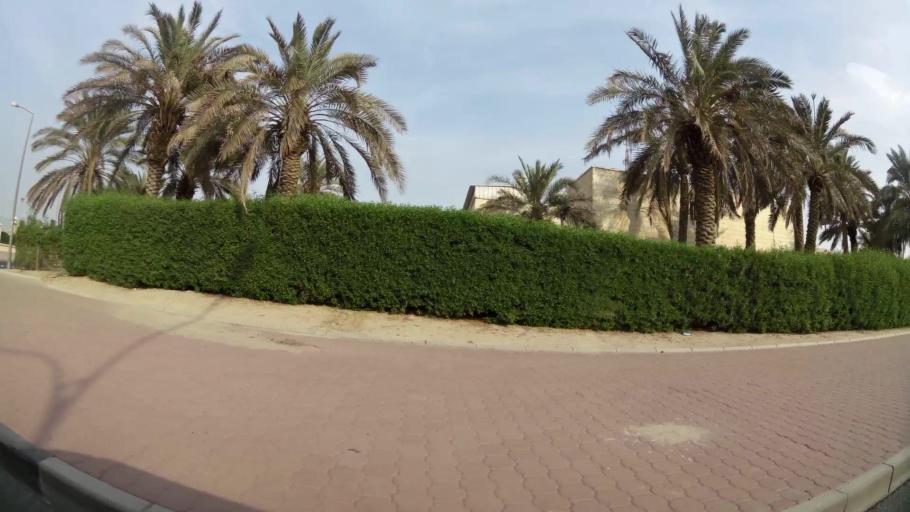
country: KW
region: Al Farwaniyah
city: Janub as Surrah
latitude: 29.2806
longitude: 47.9775
